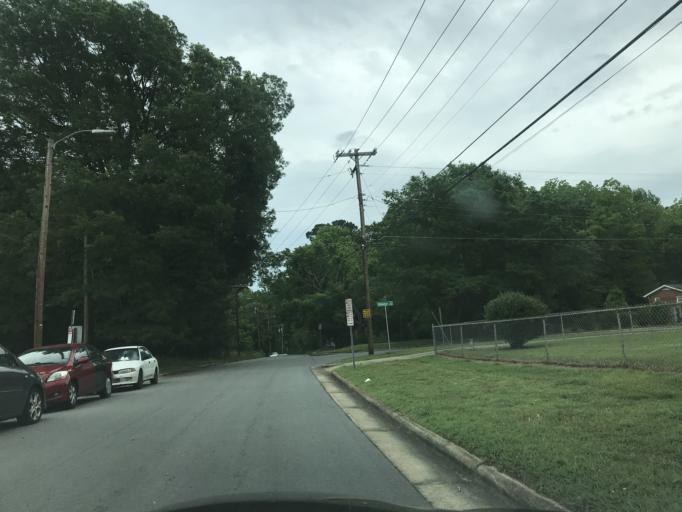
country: US
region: North Carolina
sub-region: Wake County
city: West Raleigh
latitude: 35.7917
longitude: -78.6909
